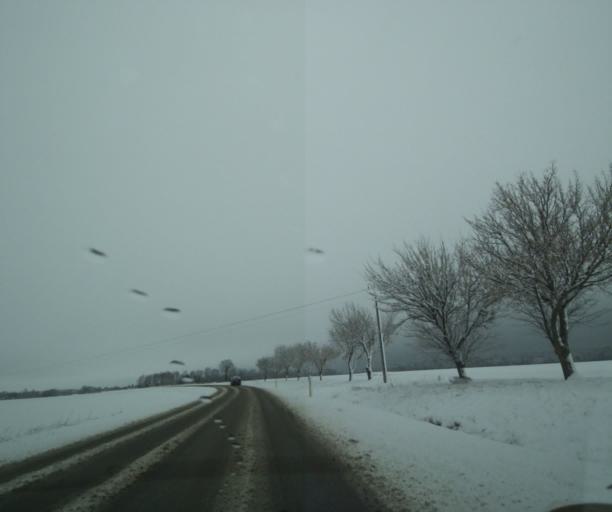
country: FR
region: Champagne-Ardenne
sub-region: Departement de la Haute-Marne
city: Wassy
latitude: 48.5368
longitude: 4.9251
